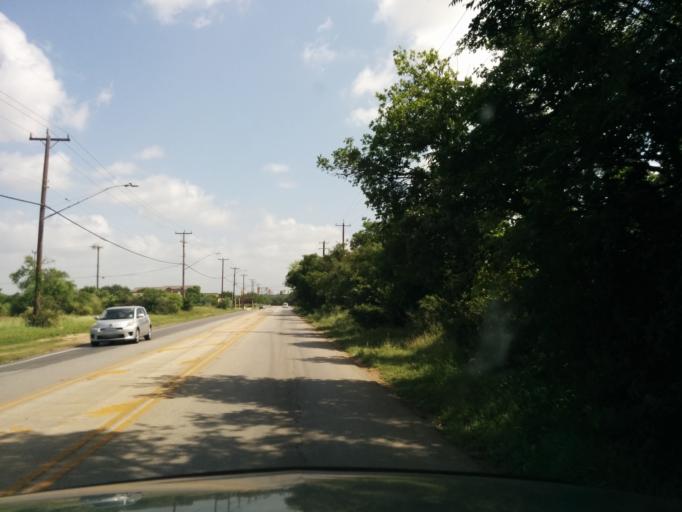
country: US
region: Texas
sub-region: Bexar County
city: Helotes
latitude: 29.5754
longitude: -98.6317
